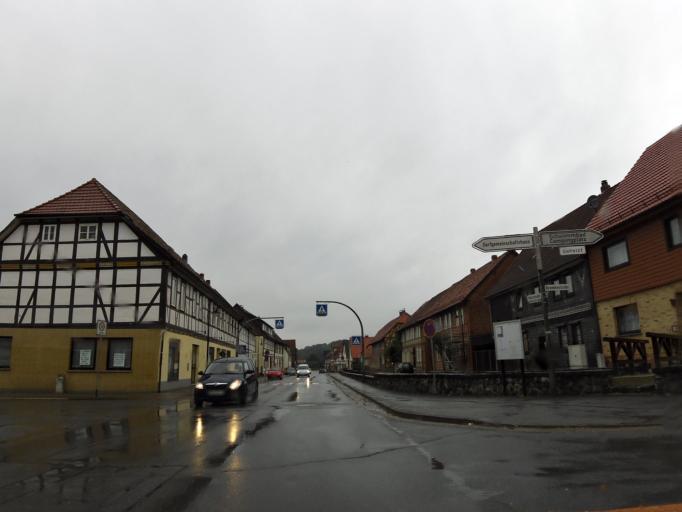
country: DE
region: Lower Saxony
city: Herzberg am Harz
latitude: 51.6285
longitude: 10.3784
